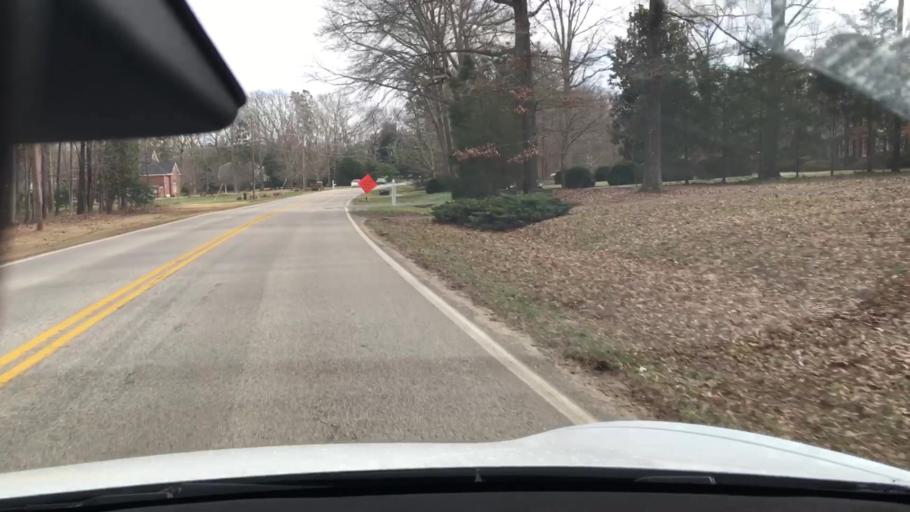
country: US
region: Virginia
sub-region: Chesterfield County
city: Bon Air
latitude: 37.5272
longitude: -77.6501
